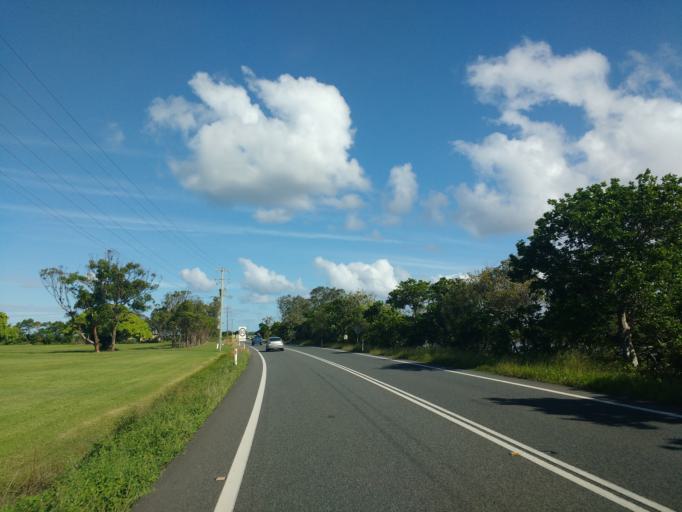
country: AU
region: New South Wales
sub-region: Richmond Valley
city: Evans Head
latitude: -28.9855
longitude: 153.4620
